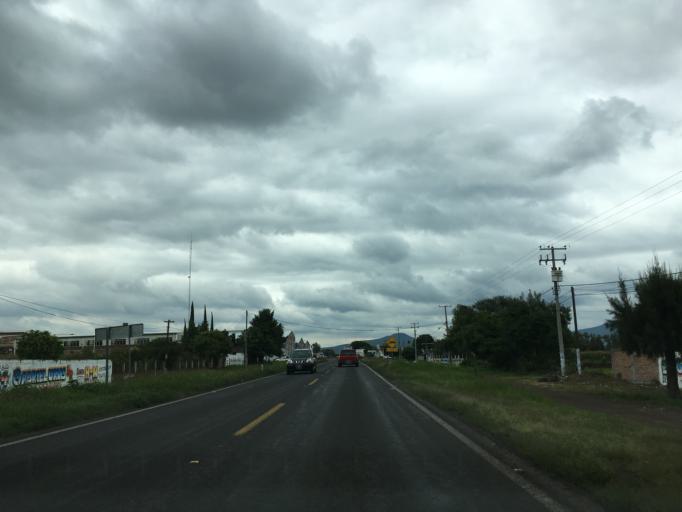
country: MX
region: Michoacan
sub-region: Cuitzeo
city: Cuamio
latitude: 20.0361
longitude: -101.1522
